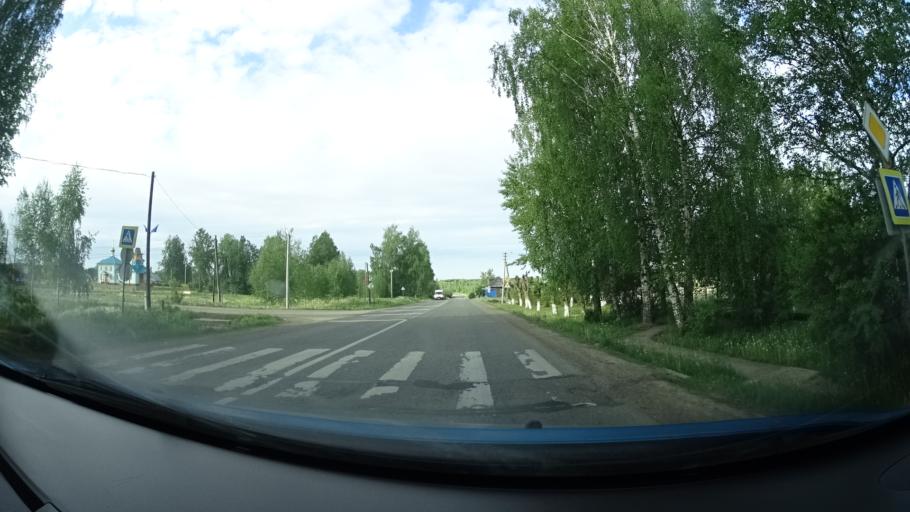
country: RU
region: Perm
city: Osa
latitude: 57.3705
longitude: 55.6083
